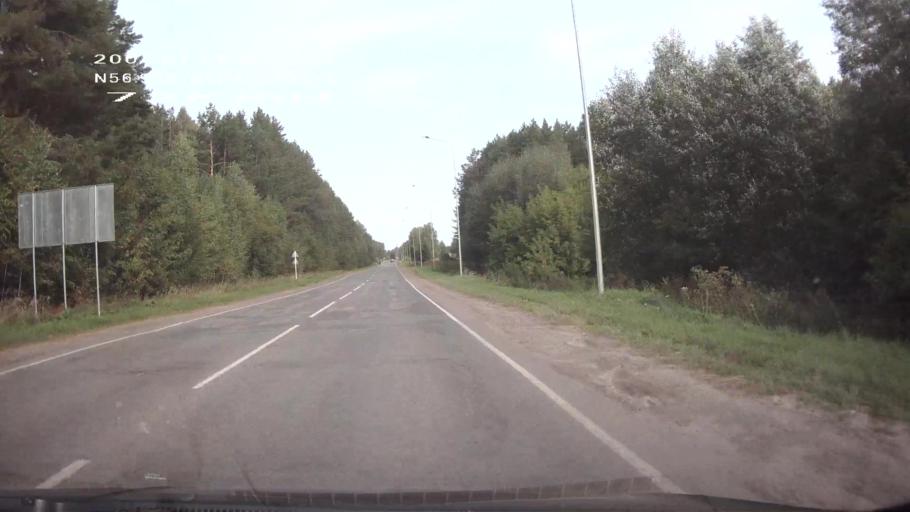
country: RU
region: Mariy-El
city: Kuzhener
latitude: 56.9868
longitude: 48.7444
